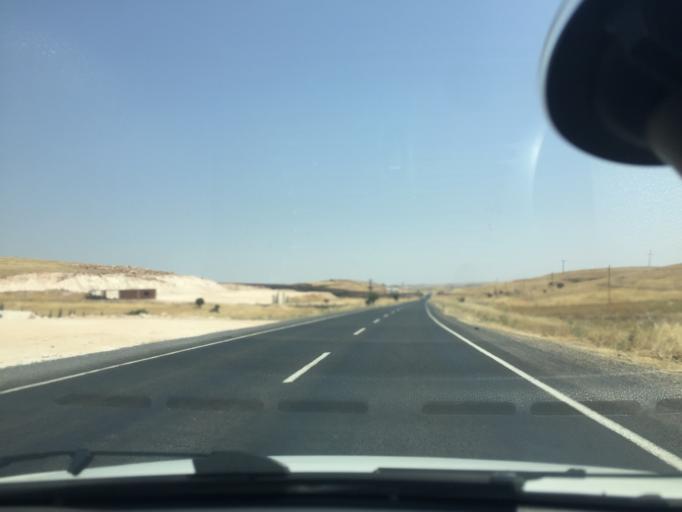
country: TR
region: Mardin
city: Kindirip
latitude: 37.4628
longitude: 41.2302
